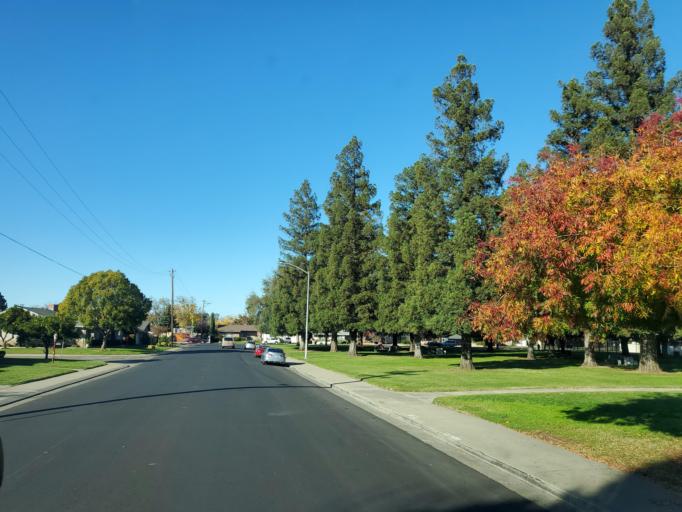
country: US
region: California
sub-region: San Joaquin County
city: Lincoln Village
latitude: 38.0005
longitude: -121.3109
